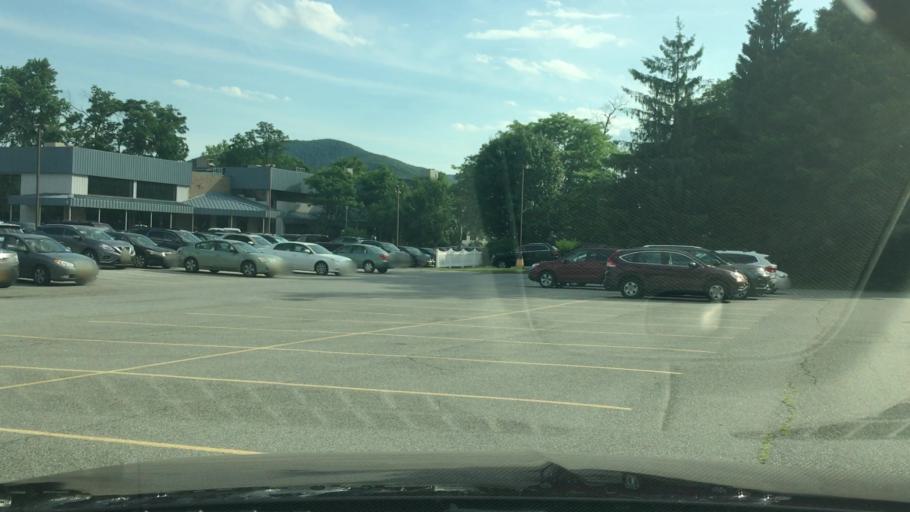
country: US
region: New York
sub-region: Dutchess County
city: Fishkill
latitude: 41.5359
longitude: -73.8947
